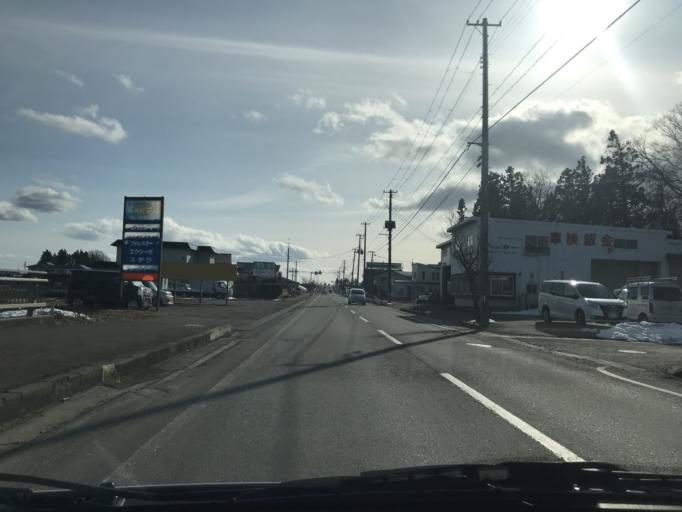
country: JP
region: Iwate
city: Kitakami
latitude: 39.3003
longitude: 141.0984
